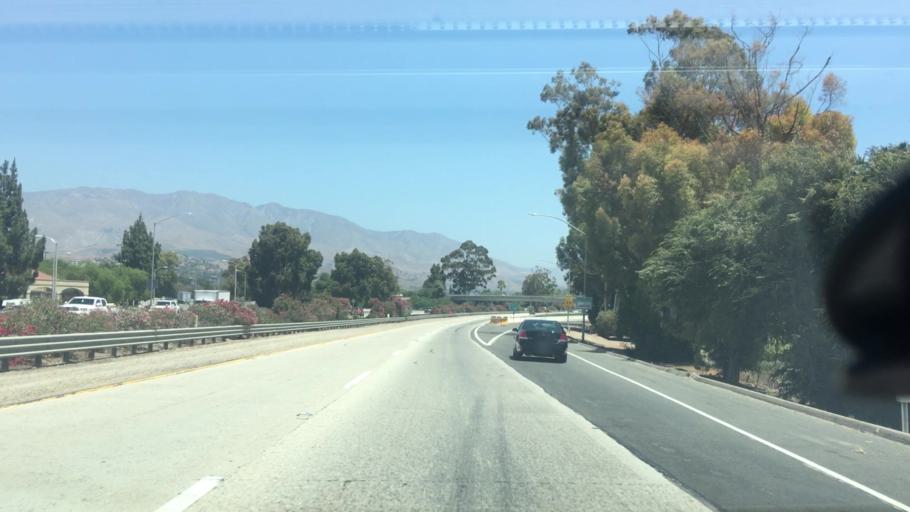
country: US
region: California
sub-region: Ventura County
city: Santa Paula
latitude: 34.3347
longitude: -119.0861
